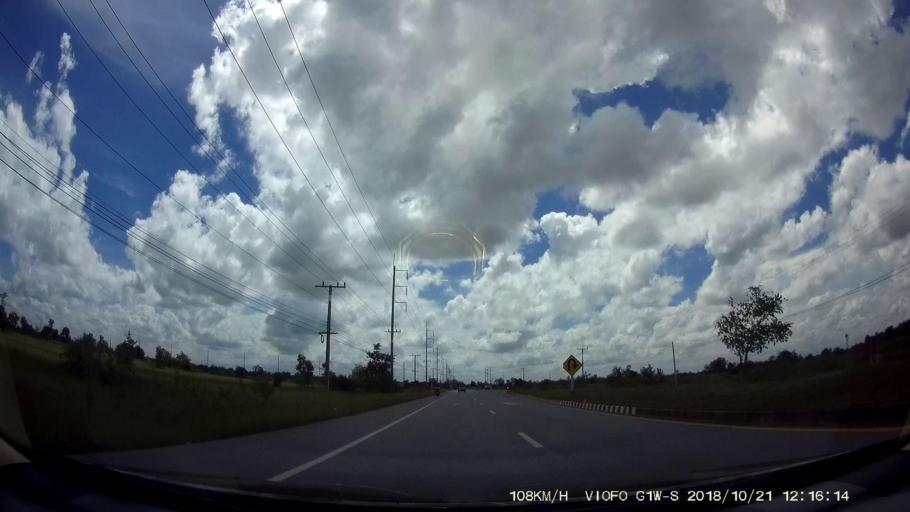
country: TH
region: Nakhon Ratchasima
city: Dan Khun Thot
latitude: 15.3510
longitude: 101.8270
